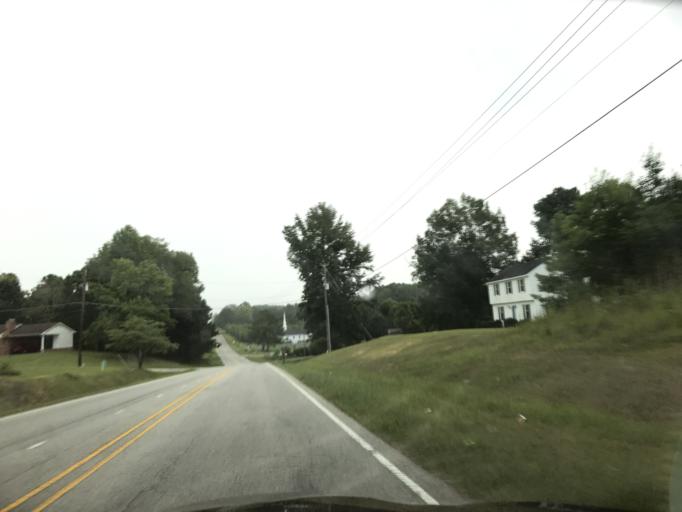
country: US
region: North Carolina
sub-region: Johnston County
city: Wilsons Mills
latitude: 35.5574
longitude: -78.3817
